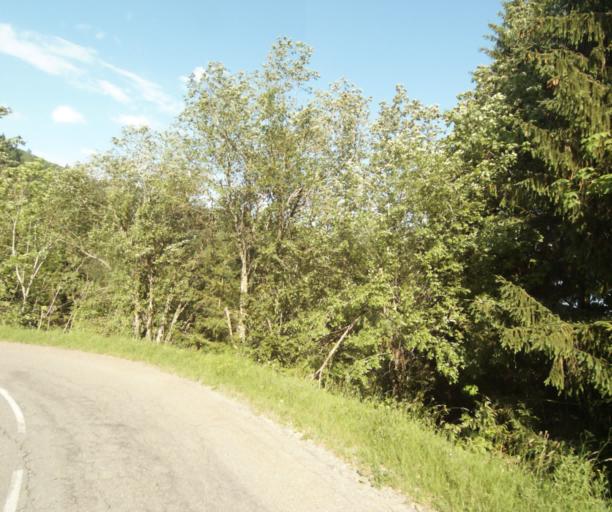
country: FR
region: Rhone-Alpes
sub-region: Departement de la Haute-Savoie
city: Lyaud
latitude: 46.3003
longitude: 6.5057
